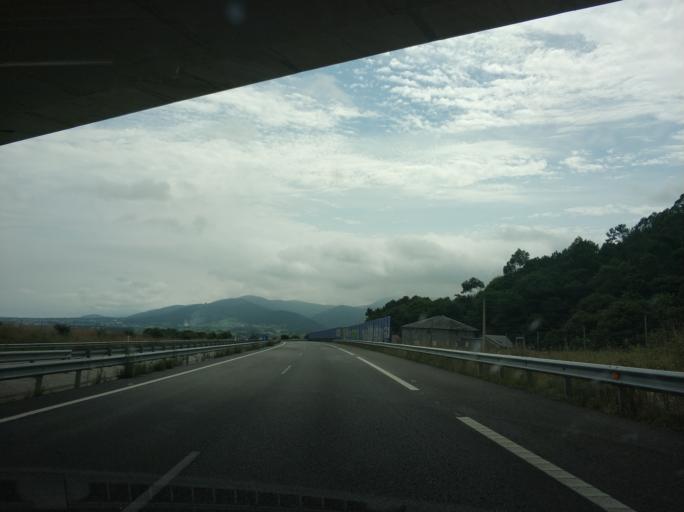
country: ES
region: Asturias
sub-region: Province of Asturias
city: Navia
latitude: 43.5293
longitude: -6.5776
